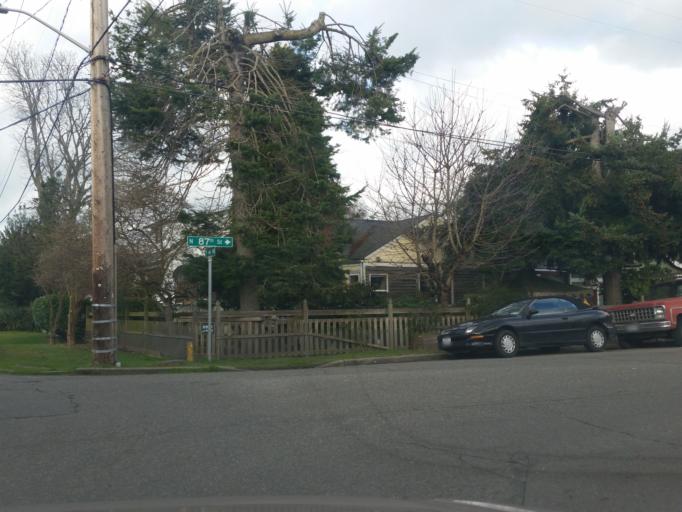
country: US
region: Washington
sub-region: King County
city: Shoreline
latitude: 47.6924
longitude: -122.3579
